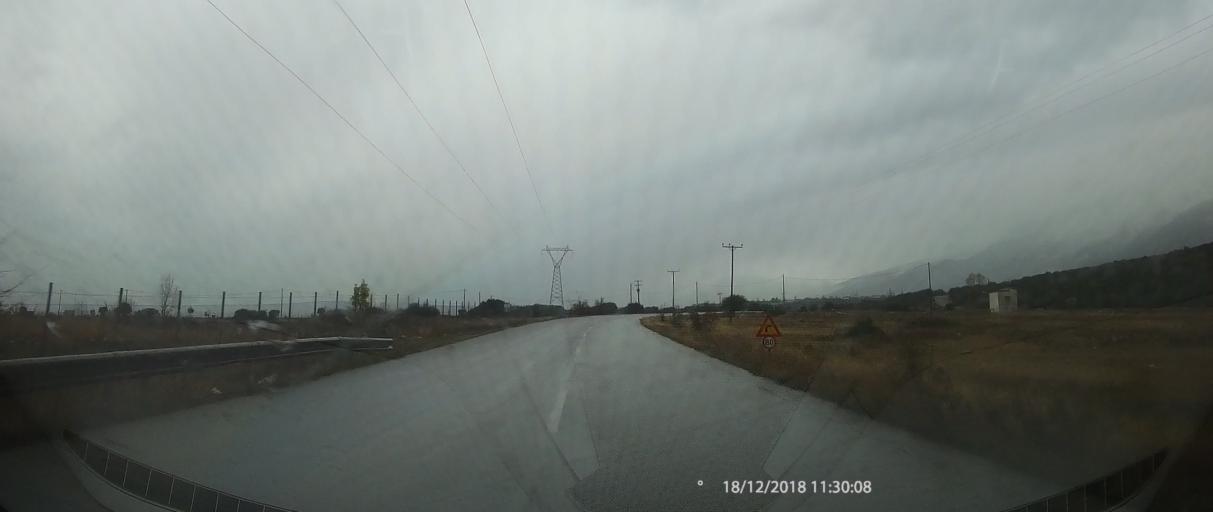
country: GR
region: Central Macedonia
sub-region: Nomos Pierias
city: Litochoro
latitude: 40.1267
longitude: 22.5227
